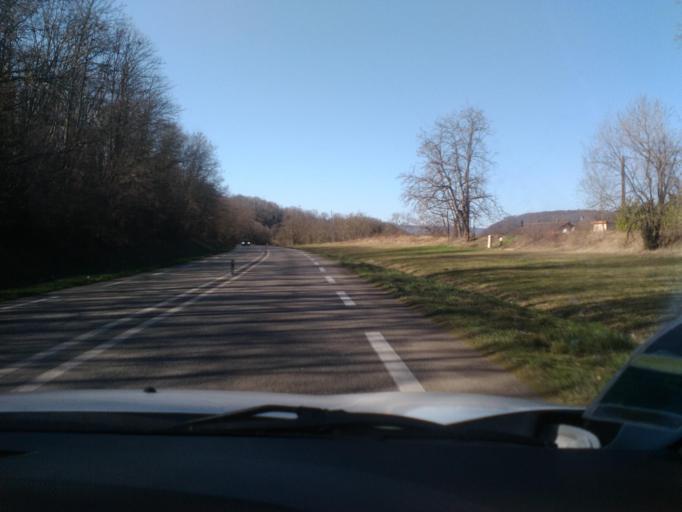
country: FR
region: Alsace
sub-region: Departement du Bas-Rhin
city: Mutzig
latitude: 48.5283
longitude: 7.4611
